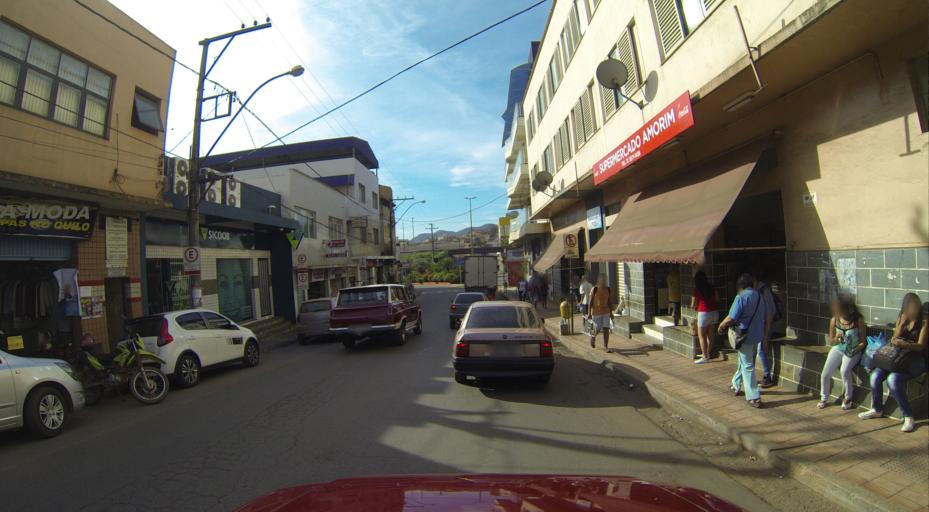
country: BR
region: Minas Gerais
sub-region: Brumadinho
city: Brumadinho
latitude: -20.1426
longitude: -44.2012
